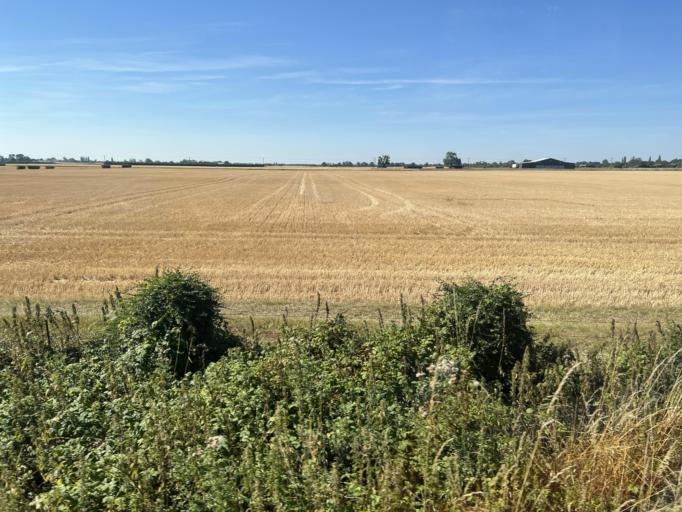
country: GB
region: England
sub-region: Lincolnshire
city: Heckington
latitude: 52.9744
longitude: -0.2781
